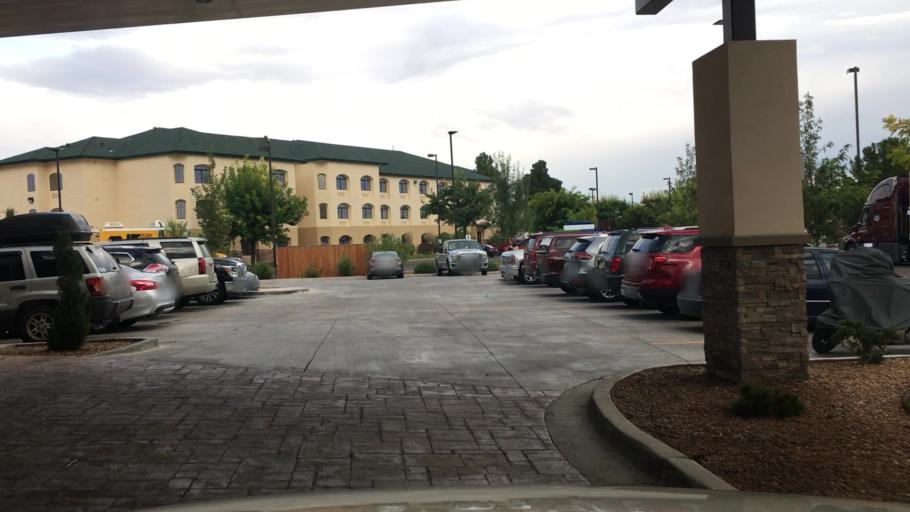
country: US
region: New Mexico
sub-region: Chaves County
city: Roswell
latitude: 33.4201
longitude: -104.5249
